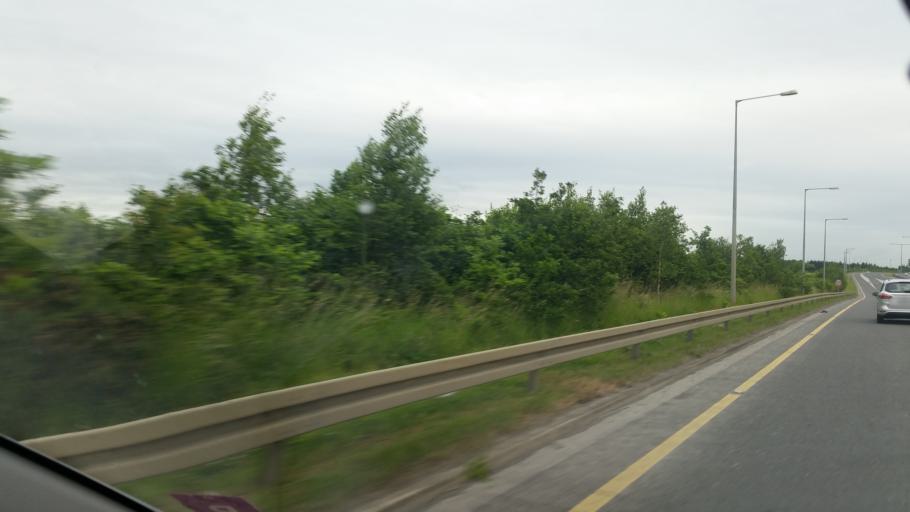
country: IE
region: Leinster
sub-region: Fingal County
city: Blanchardstown
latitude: 53.4317
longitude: -6.3424
